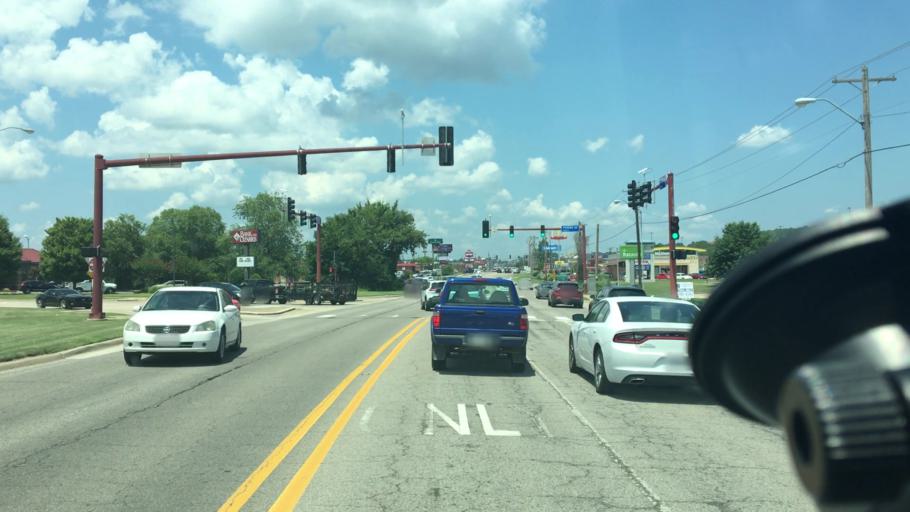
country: US
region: Arkansas
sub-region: Sebastian County
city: Barling
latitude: 35.3465
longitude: -94.3368
